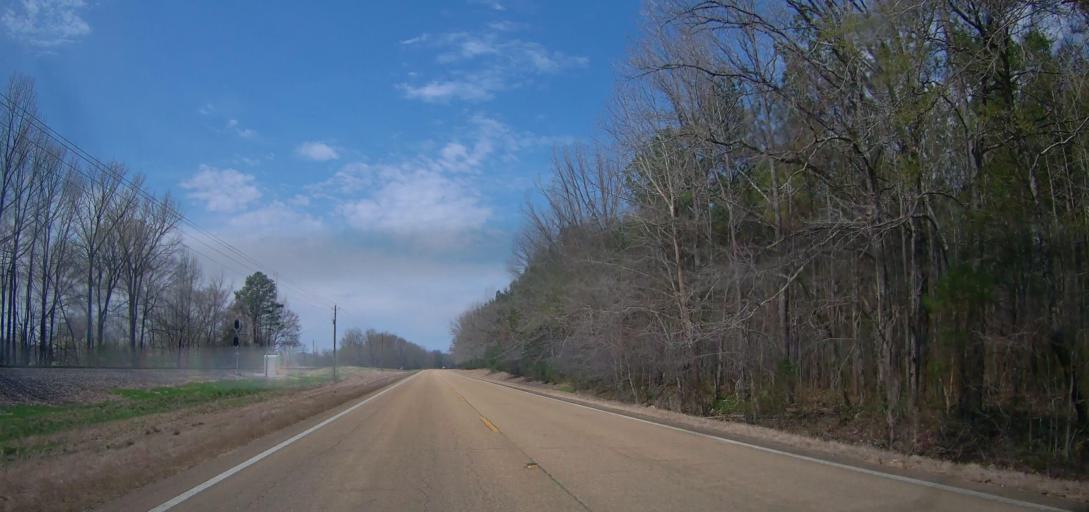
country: US
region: Mississippi
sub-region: Benton County
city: Ashland
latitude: 34.6261
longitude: -89.2561
